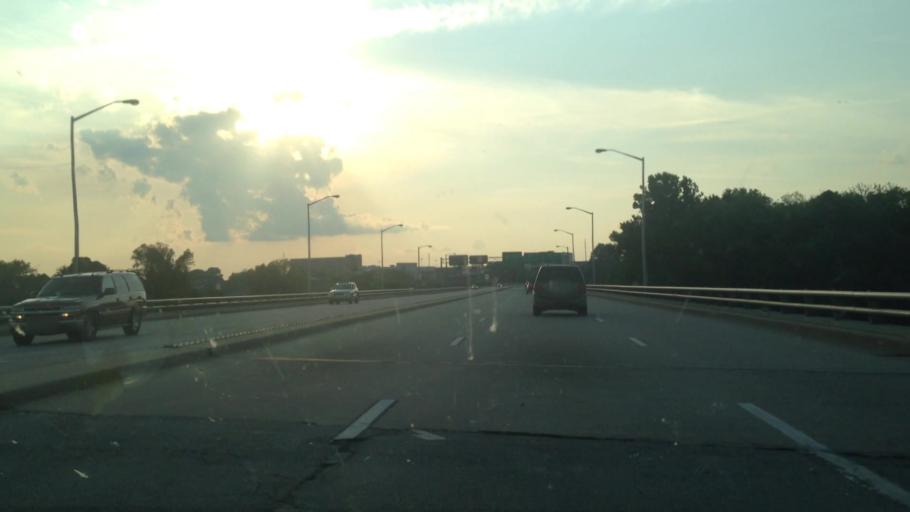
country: US
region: Virginia
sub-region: City of Danville
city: Danville
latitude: 36.5895
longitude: -79.4120
